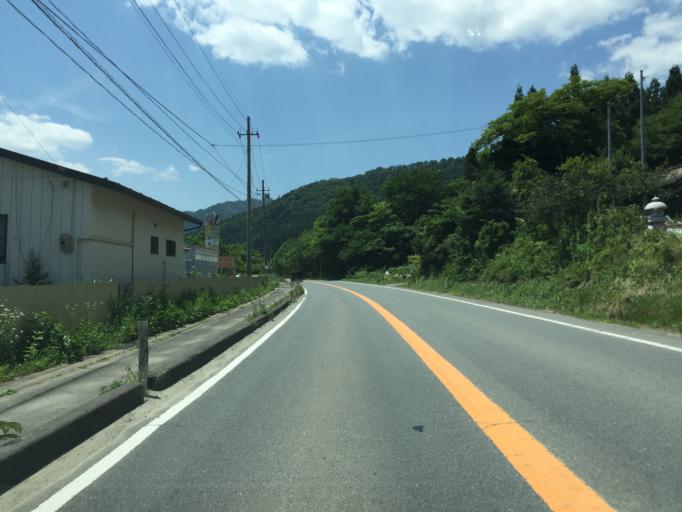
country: JP
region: Miyagi
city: Marumori
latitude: 37.7730
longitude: 140.8630
